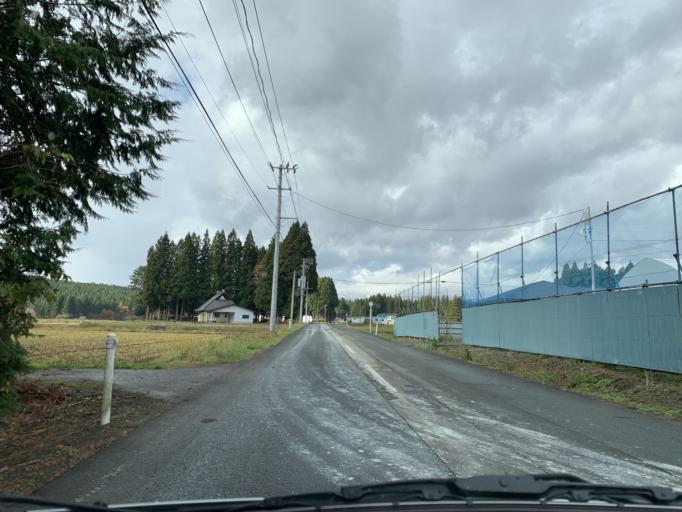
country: JP
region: Iwate
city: Mizusawa
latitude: 39.0865
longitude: 141.0241
